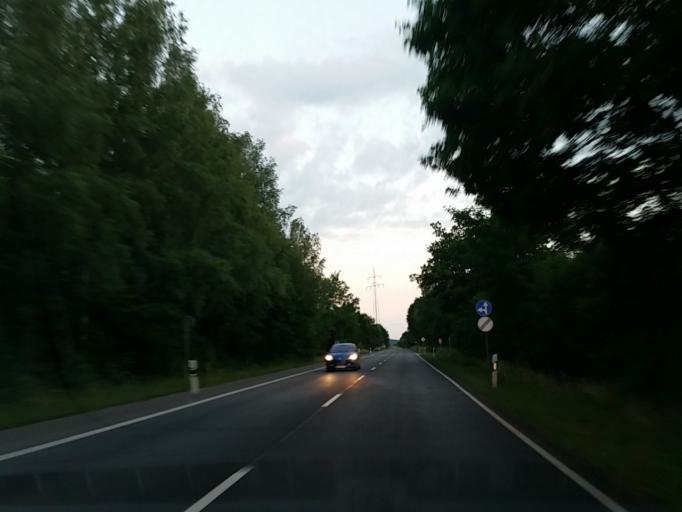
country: DE
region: Saarland
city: Wadern
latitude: 49.5253
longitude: 6.8757
